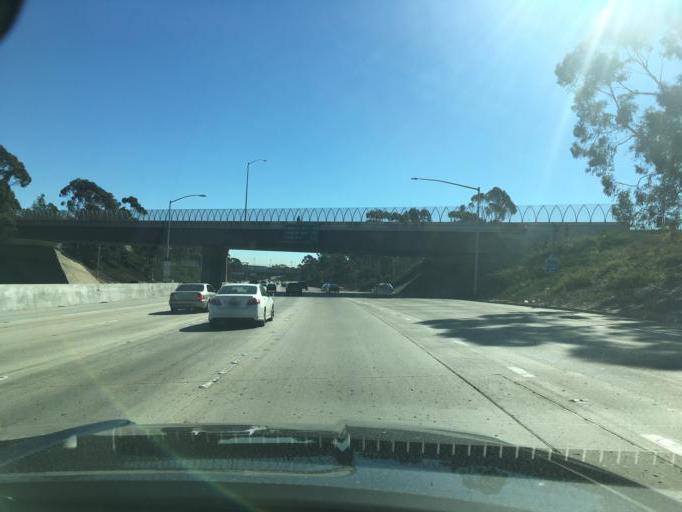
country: US
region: California
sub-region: San Diego County
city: National City
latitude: 32.7122
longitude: -117.1018
